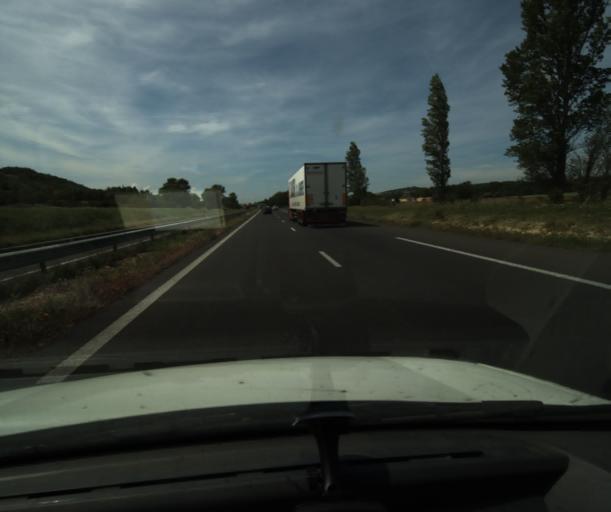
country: FR
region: Midi-Pyrenees
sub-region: Departement de la Haute-Garonne
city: Avignonet-Lauragais
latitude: 43.3343
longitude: 1.8408
